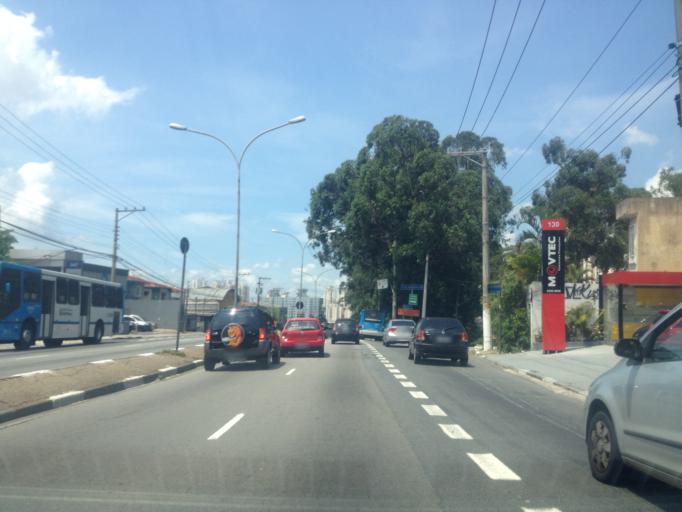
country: BR
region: Sao Paulo
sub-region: Diadema
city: Diadema
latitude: -23.6542
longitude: -46.6799
